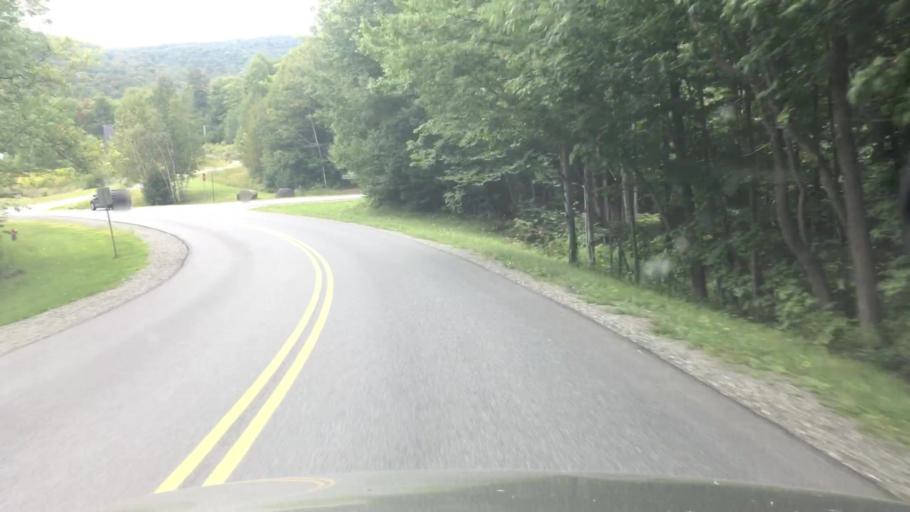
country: US
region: Vermont
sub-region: Windham County
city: Dover
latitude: 42.9725
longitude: -72.8946
